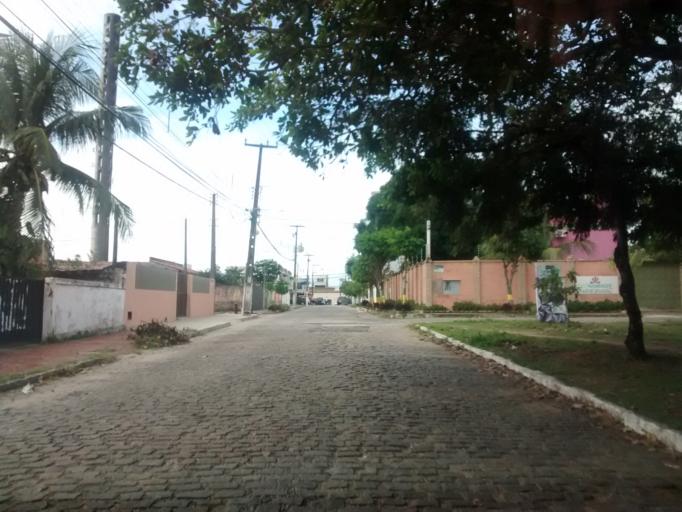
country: BR
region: Rio Grande do Norte
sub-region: Natal
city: Natal
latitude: -5.8742
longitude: -35.1818
